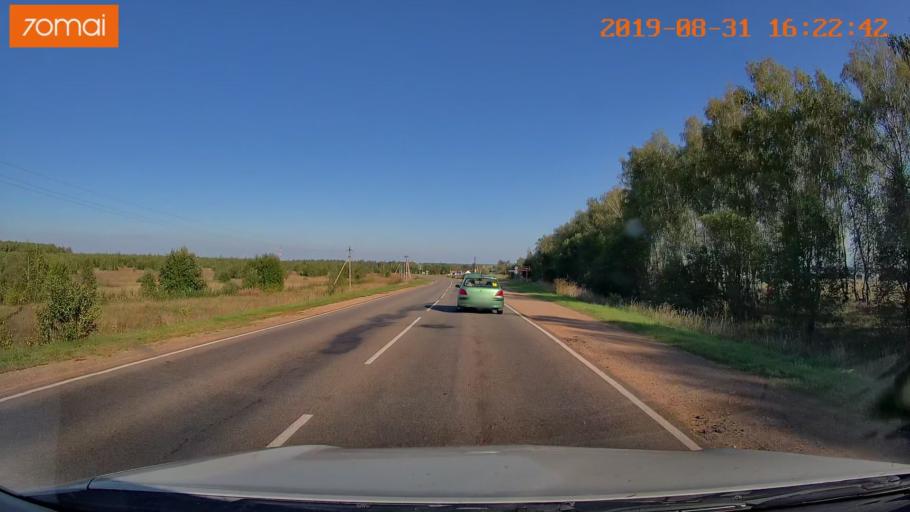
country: RU
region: Kaluga
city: Babynino
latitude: 54.5195
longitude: 35.6649
